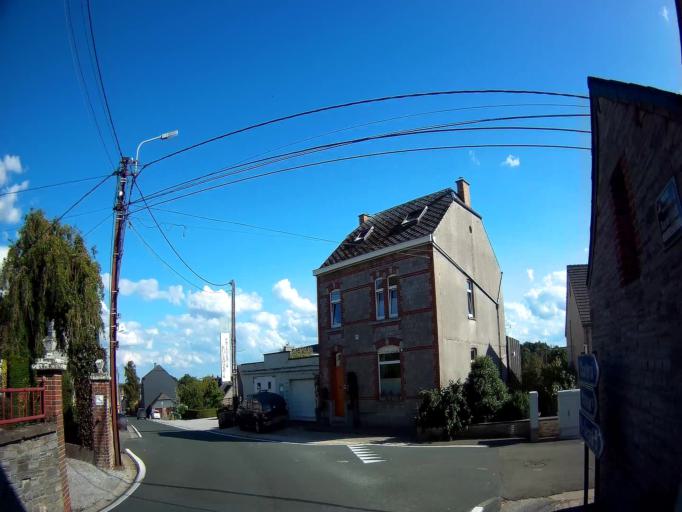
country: BE
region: Wallonia
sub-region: Province de Namur
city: Mettet
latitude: 50.3187
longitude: 4.7496
